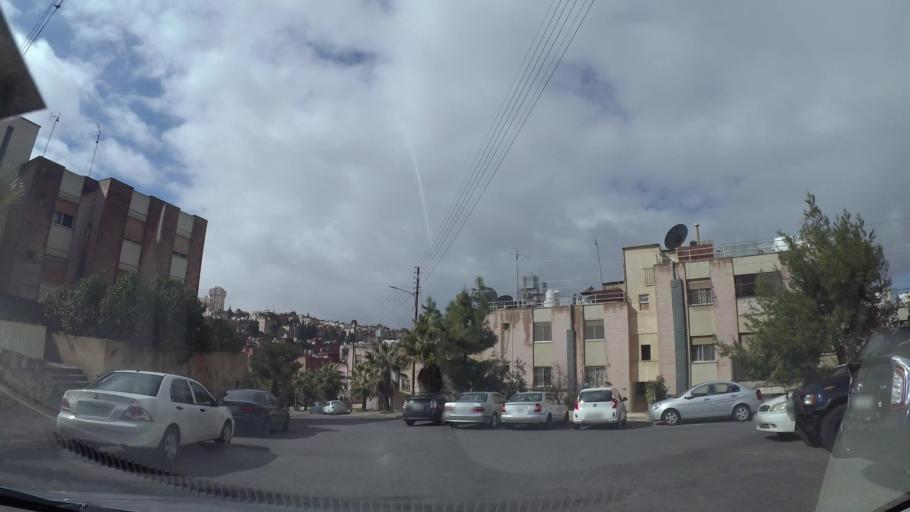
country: JO
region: Amman
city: Al Jubayhah
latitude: 32.0538
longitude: 35.8768
